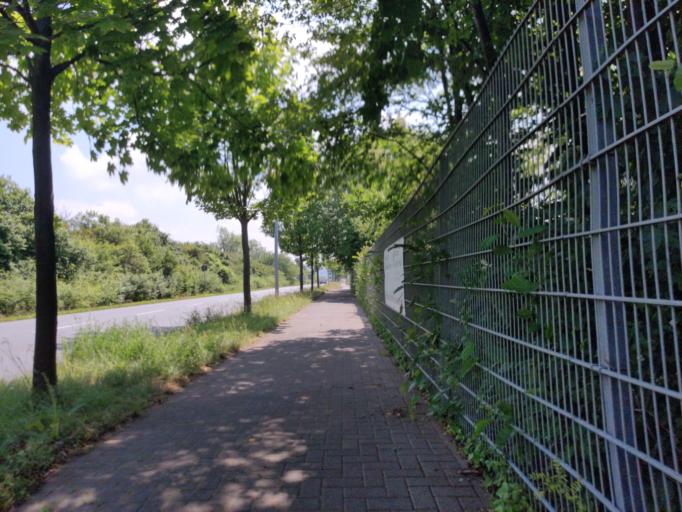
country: DE
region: Lower Saxony
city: Hildesheim
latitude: 52.1646
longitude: 9.9976
